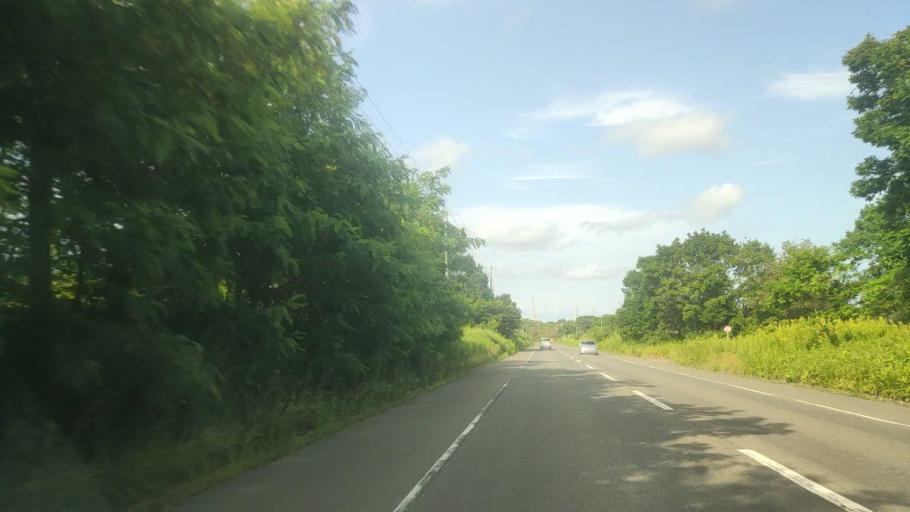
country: JP
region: Hokkaido
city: Tomakomai
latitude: 42.6970
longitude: 141.7383
